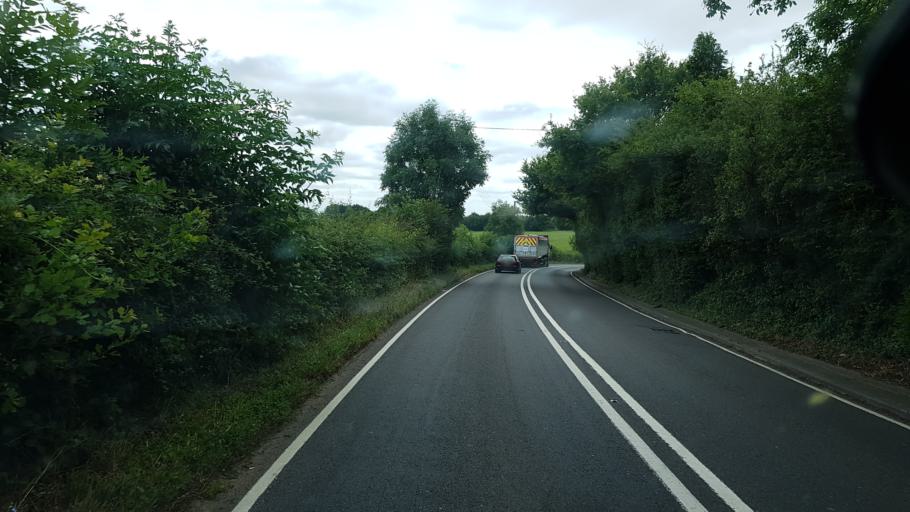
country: GB
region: England
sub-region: Surrey
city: Godstone
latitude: 51.2254
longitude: -0.0470
